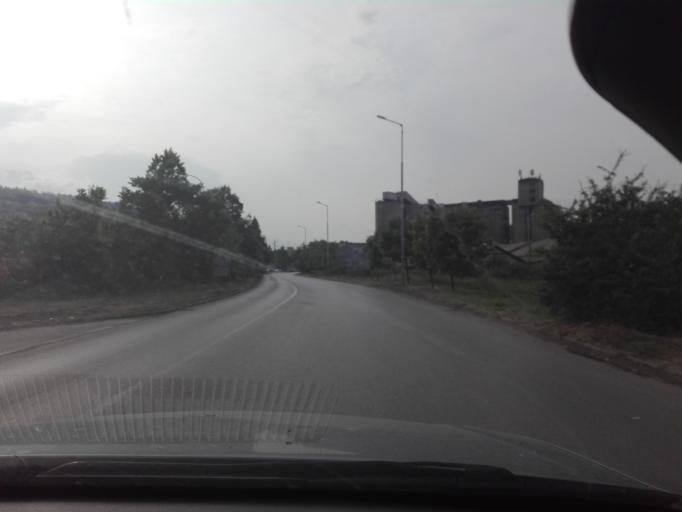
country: MK
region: Bitola
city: Bitola
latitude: 41.0141
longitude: 21.3471
